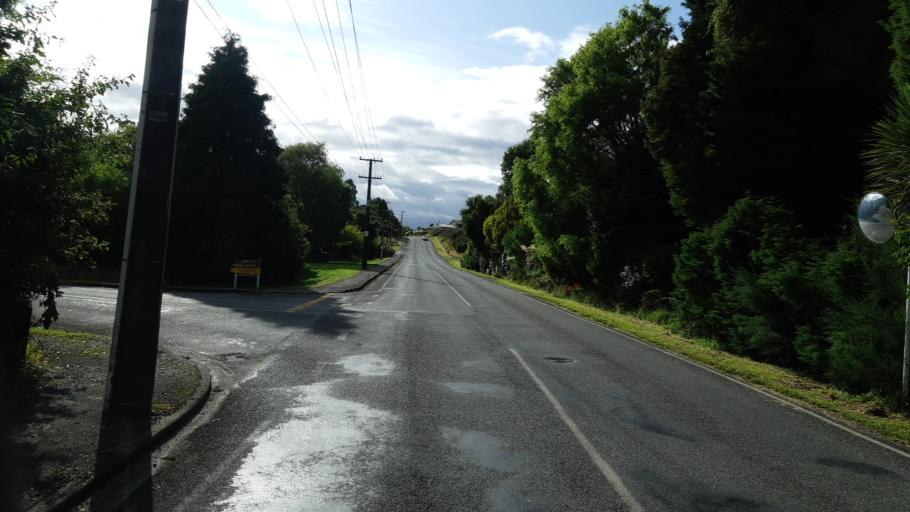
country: NZ
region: West Coast
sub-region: Westland District
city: Hokitika
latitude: -42.7470
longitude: 171.0034
